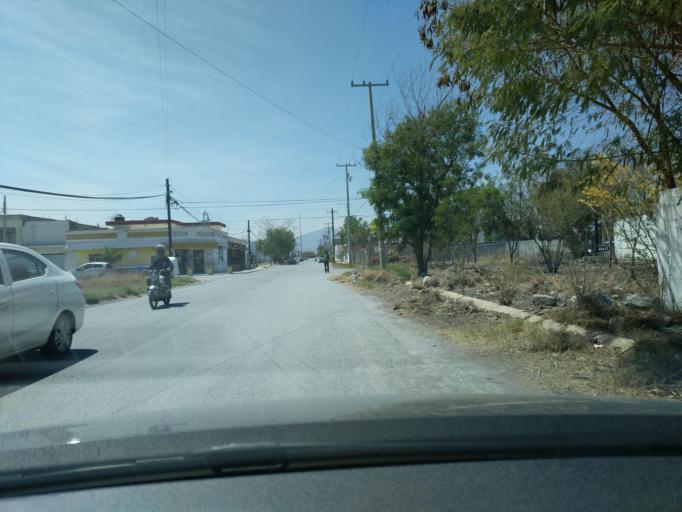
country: MX
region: Nuevo Leon
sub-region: Salinas Victoria
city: Emiliano Zapata
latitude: 25.9133
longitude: -100.2639
